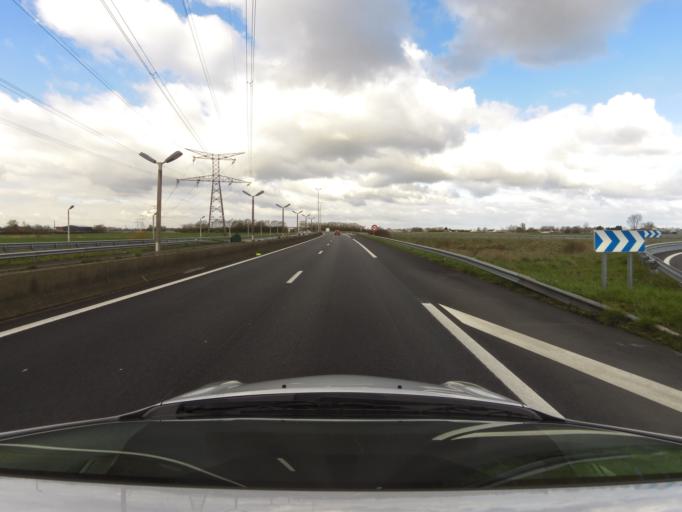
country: FR
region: Nord-Pas-de-Calais
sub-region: Departement du Pas-de-Calais
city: Saint-Folquin
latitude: 50.9518
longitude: 2.1248
